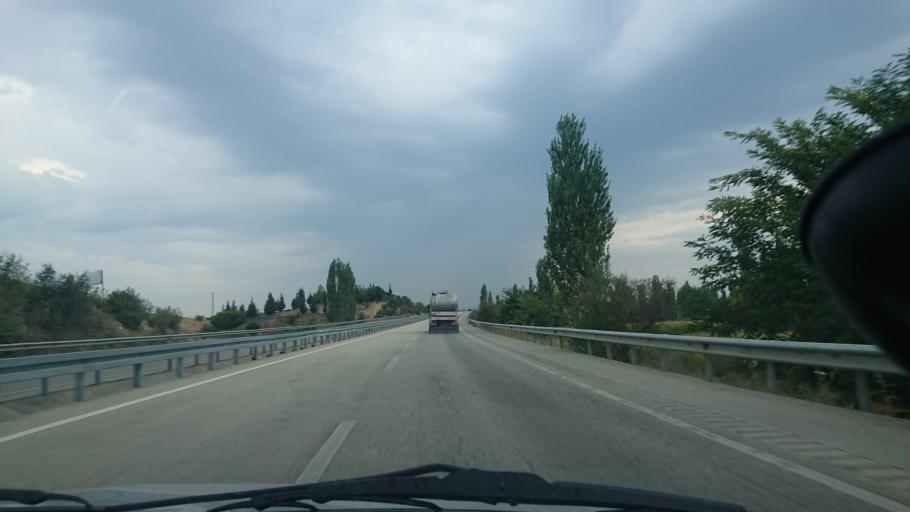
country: TR
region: Manisa
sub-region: Kula
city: Kula
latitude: 38.5891
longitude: 28.7946
